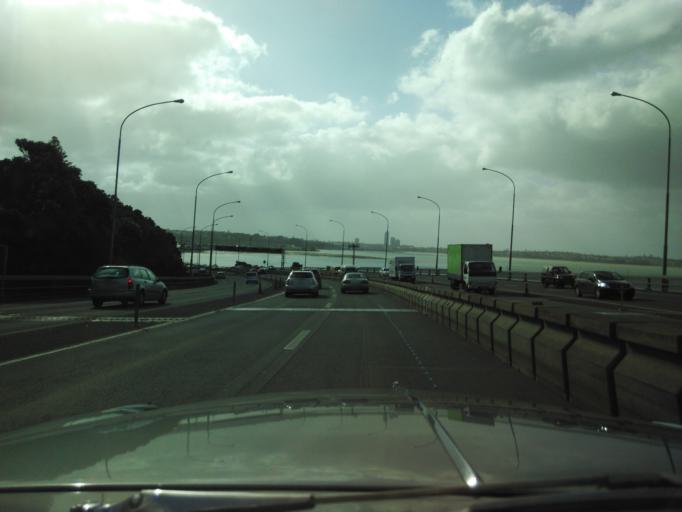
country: NZ
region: Auckland
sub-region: Auckland
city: North Shore
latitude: -36.8242
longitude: 174.7498
